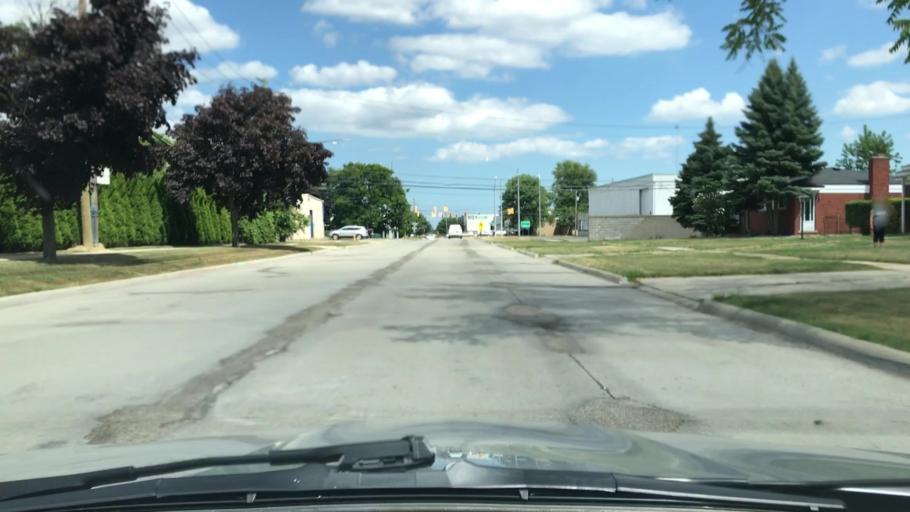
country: US
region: Michigan
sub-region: Oakland County
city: Clawson
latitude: 42.5275
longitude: -83.1221
